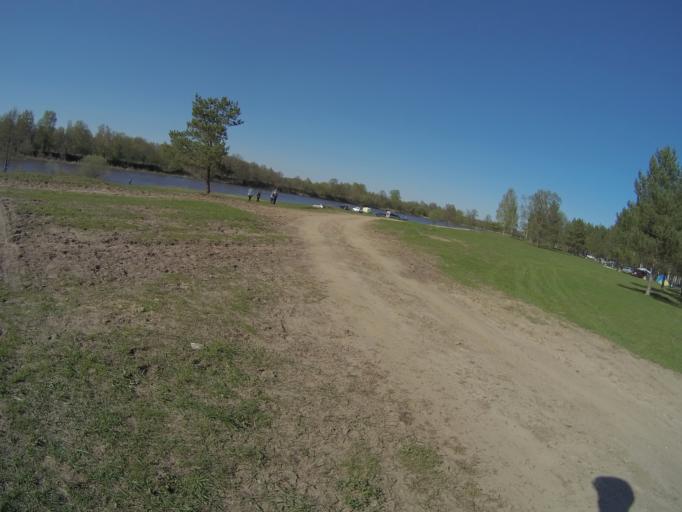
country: RU
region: Vladimir
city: Sudogda
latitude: 56.1504
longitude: 40.8206
